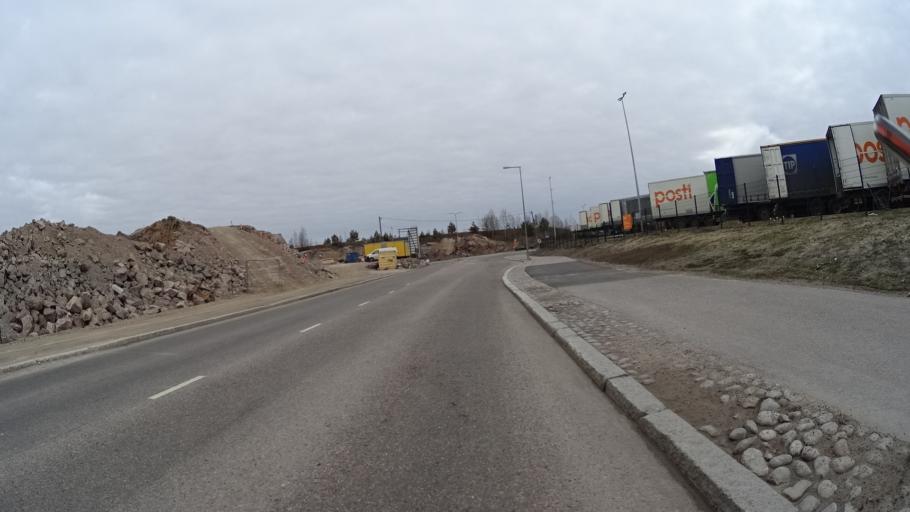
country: FI
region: Uusimaa
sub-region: Helsinki
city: Teekkarikylae
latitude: 60.3061
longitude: 24.8970
